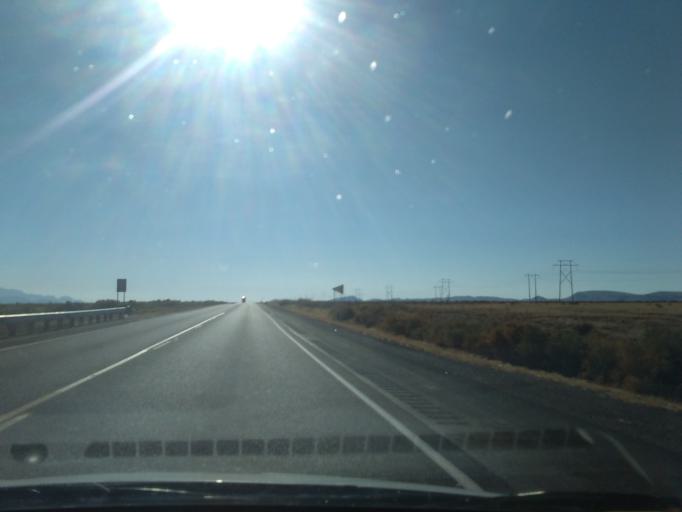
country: US
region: New Mexico
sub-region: Luna County
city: Deming
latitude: 32.4883
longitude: -107.5221
